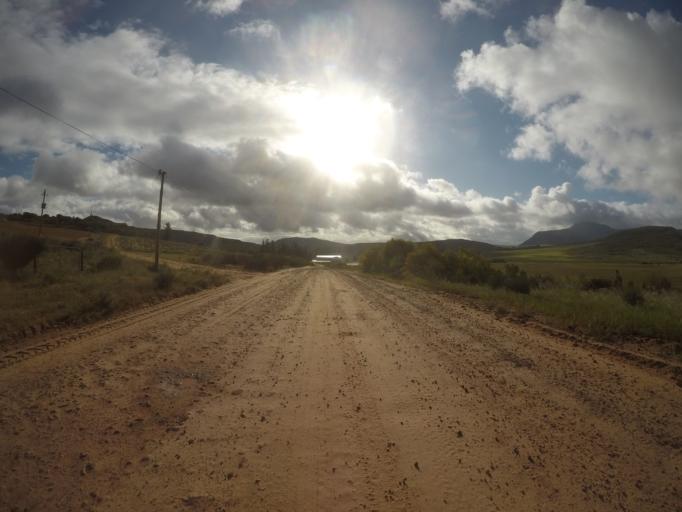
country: ZA
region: Western Cape
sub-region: West Coast District Municipality
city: Clanwilliam
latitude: -32.3429
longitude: 18.8289
